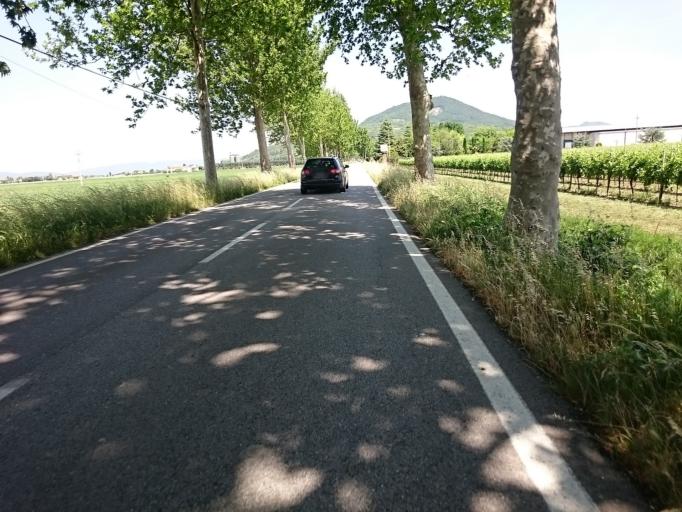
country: IT
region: Veneto
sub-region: Provincia di Padova
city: Lozzo Atestino
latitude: 45.2693
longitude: 11.6164
